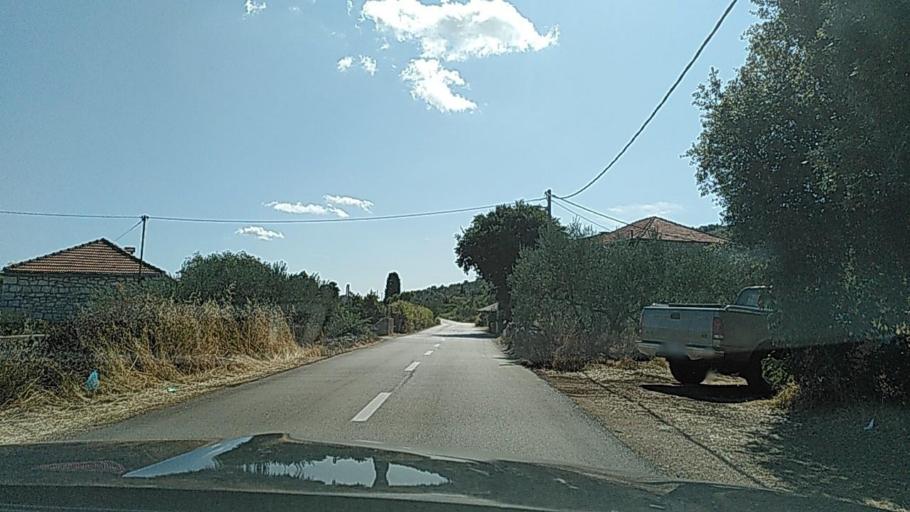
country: HR
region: Splitsko-Dalmatinska
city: Jelsa
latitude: 43.1453
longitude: 16.8356
